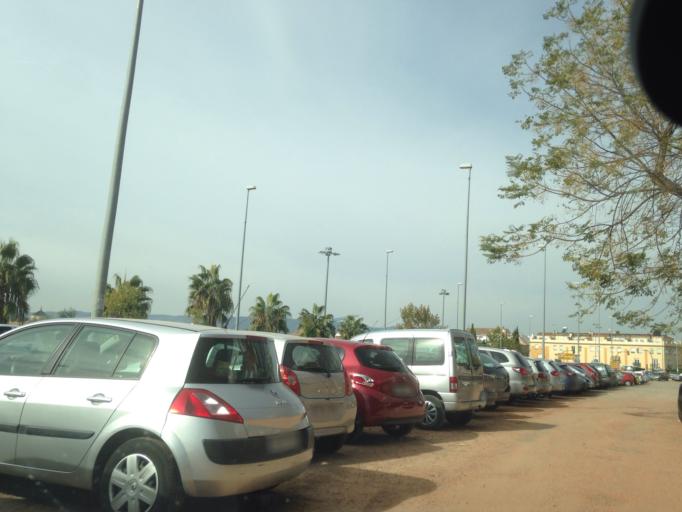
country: ES
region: Andalusia
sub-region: Province of Cordoba
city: Cordoba
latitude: 37.8791
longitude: -4.7677
